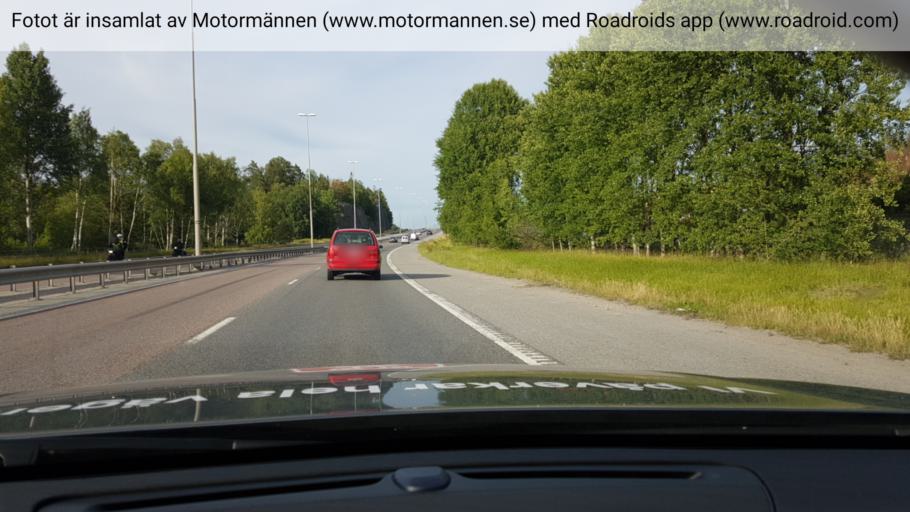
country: SE
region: Stockholm
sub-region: Huddinge Kommun
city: Huddinge
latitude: 59.2263
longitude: 17.9574
